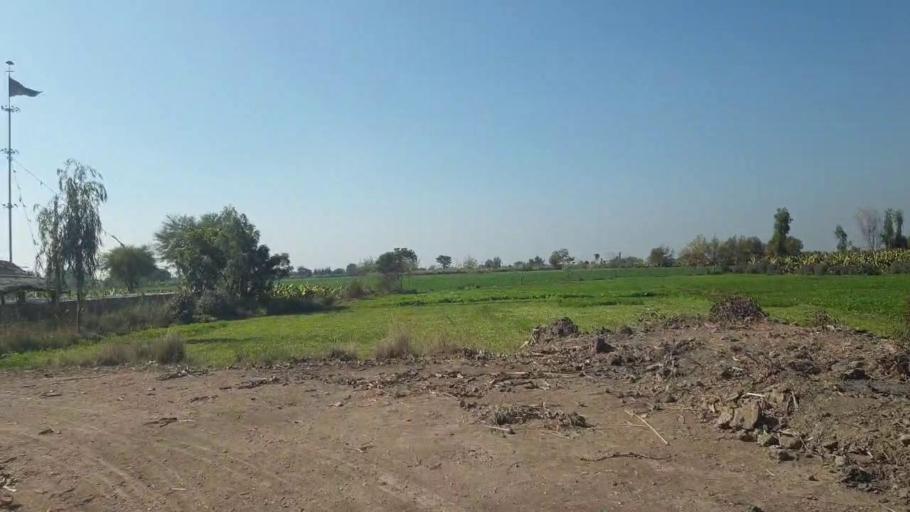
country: PK
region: Sindh
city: Shahdadpur
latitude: 25.9155
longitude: 68.5717
